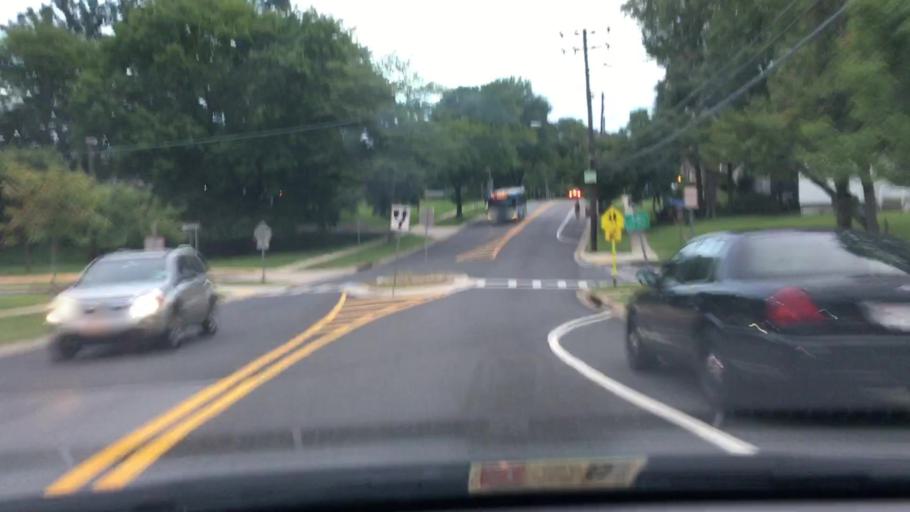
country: US
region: Maryland
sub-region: Montgomery County
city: Rockville
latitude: 39.0835
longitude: -77.1162
